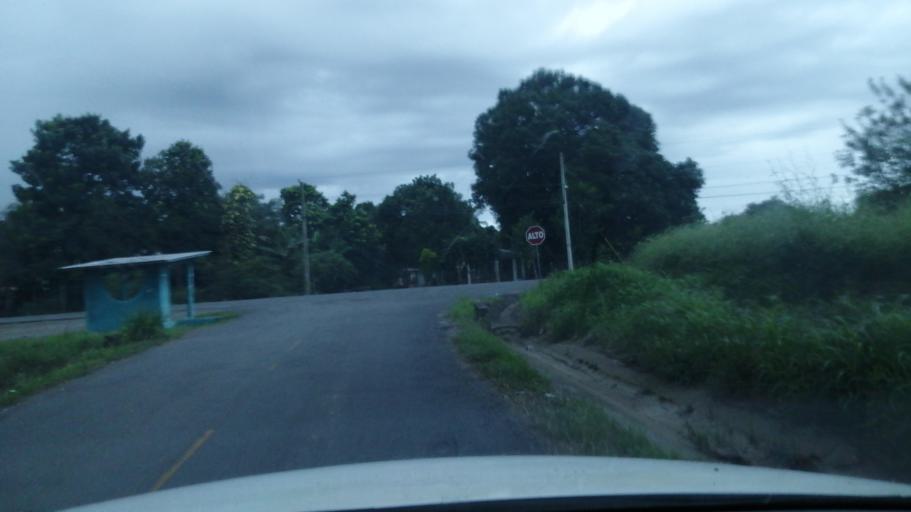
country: PA
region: Chiriqui
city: Alanje
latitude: 8.3952
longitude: -82.4958
